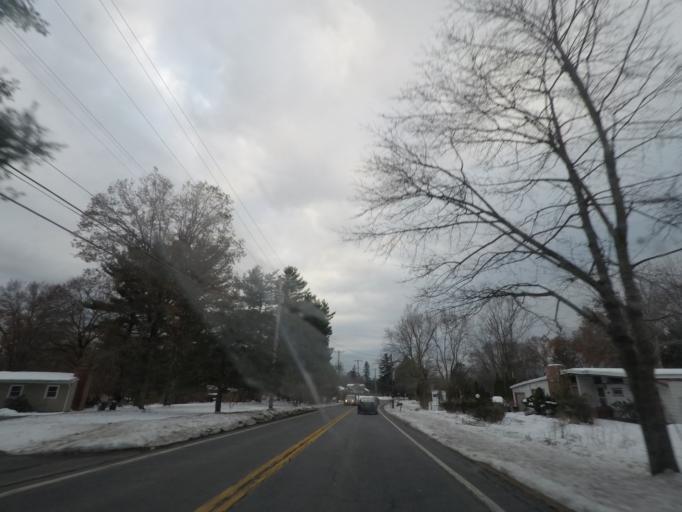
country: US
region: New York
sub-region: Ulster County
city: New Paltz
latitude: 41.7114
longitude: -74.0870
